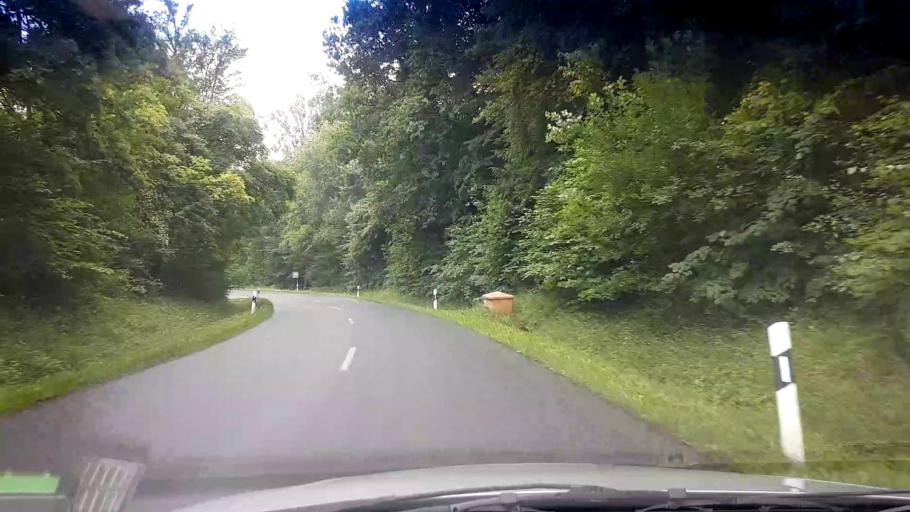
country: DE
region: Bavaria
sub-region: Upper Franconia
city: Kasendorf
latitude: 50.0724
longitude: 11.3296
